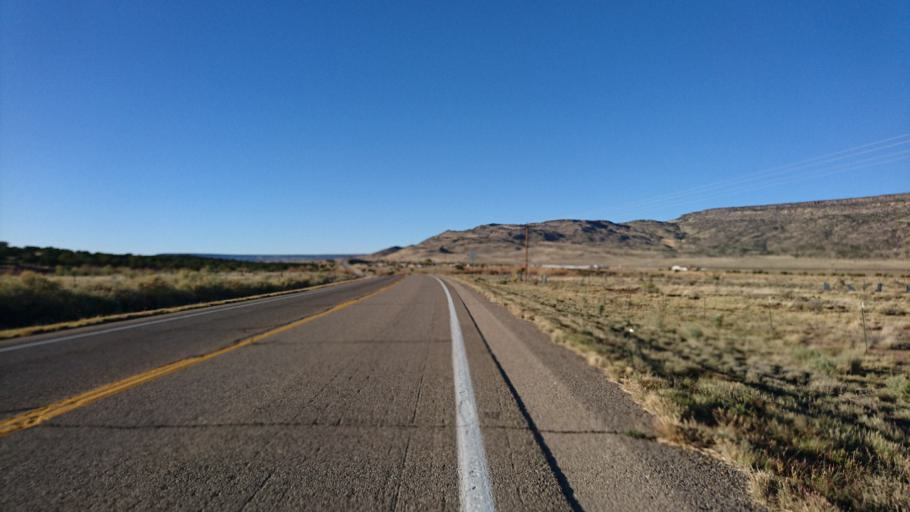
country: US
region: New Mexico
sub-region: Cibola County
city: Grants
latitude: 35.0951
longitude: -107.7719
